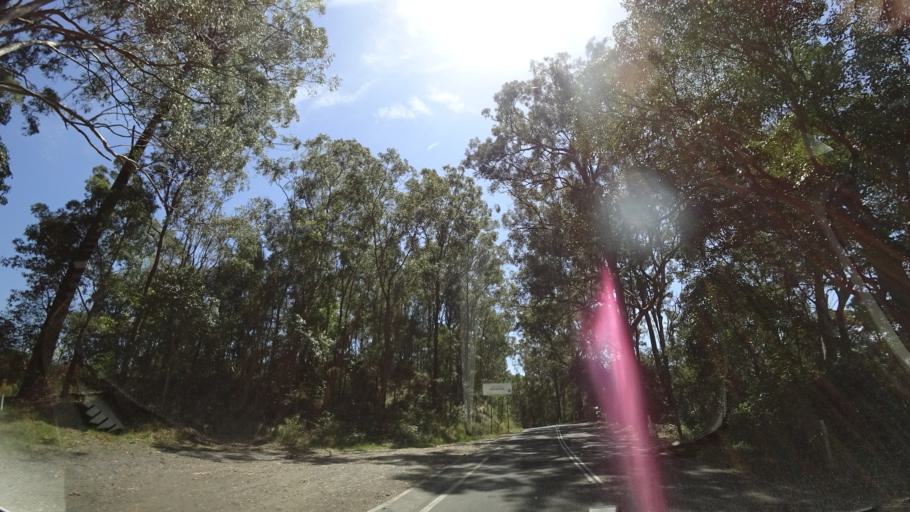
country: AU
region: Queensland
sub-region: Moreton Bay
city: Samford Valley
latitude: -27.4190
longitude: 152.8676
